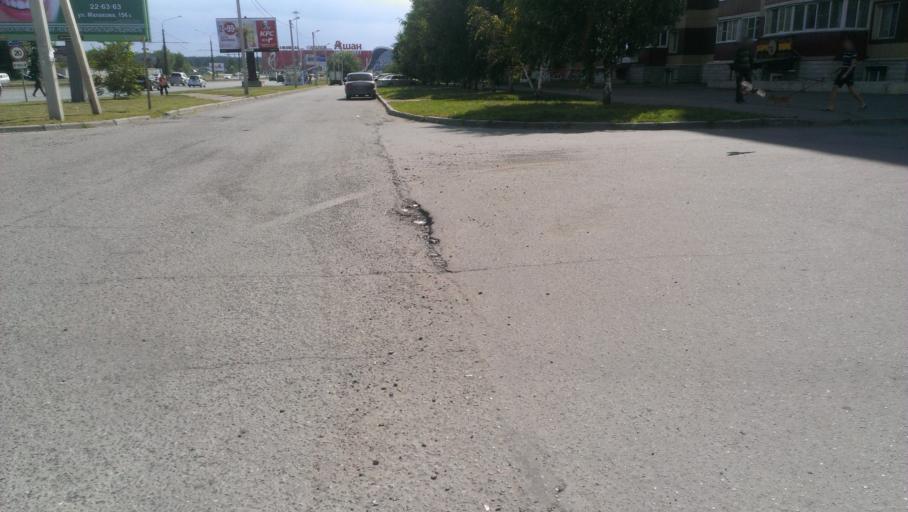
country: RU
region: Altai Krai
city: Novosilikatnyy
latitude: 53.3312
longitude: 83.6923
